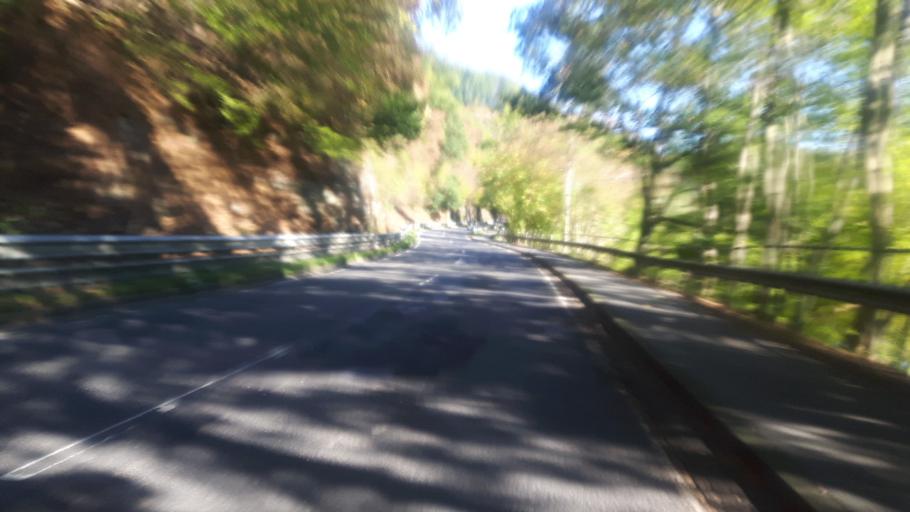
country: DE
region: Rheinland-Pfalz
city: Niederirsen
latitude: 50.8079
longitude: 7.5969
